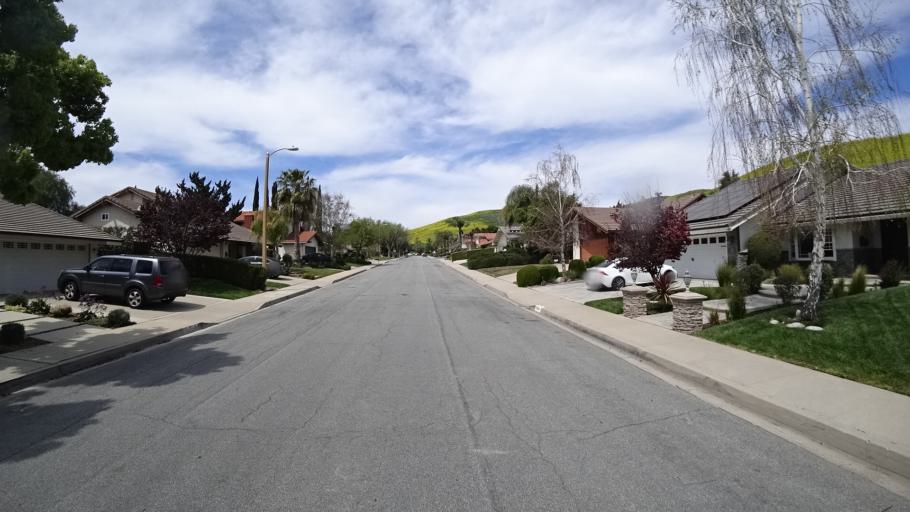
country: US
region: California
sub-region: Ventura County
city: Thousand Oaks
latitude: 34.1711
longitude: -118.8238
